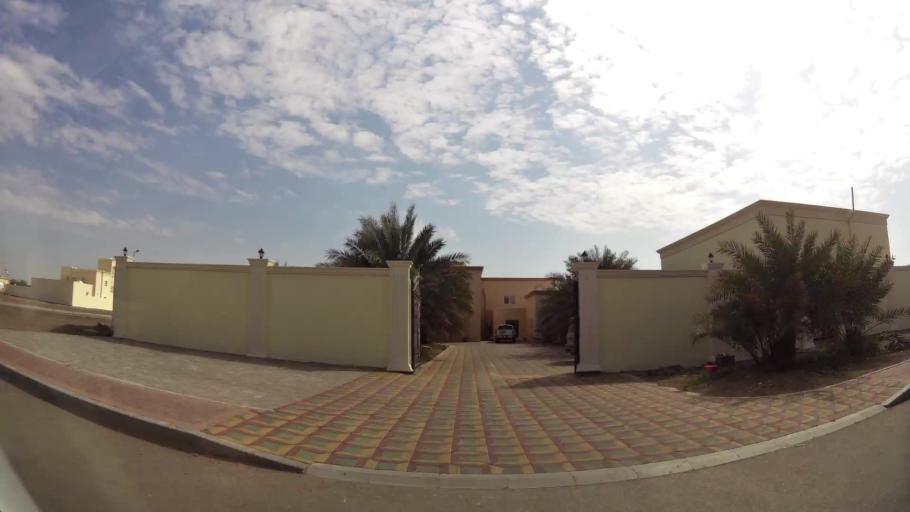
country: AE
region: Abu Dhabi
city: Al Ain
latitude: 24.1006
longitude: 55.9002
